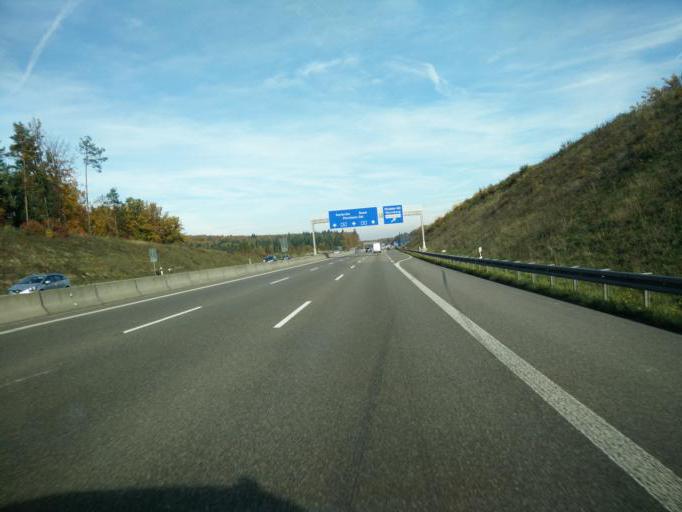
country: DE
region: Baden-Wuerttemberg
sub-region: Karlsruhe Region
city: Wurmberg
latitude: 48.8763
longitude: 8.7889
